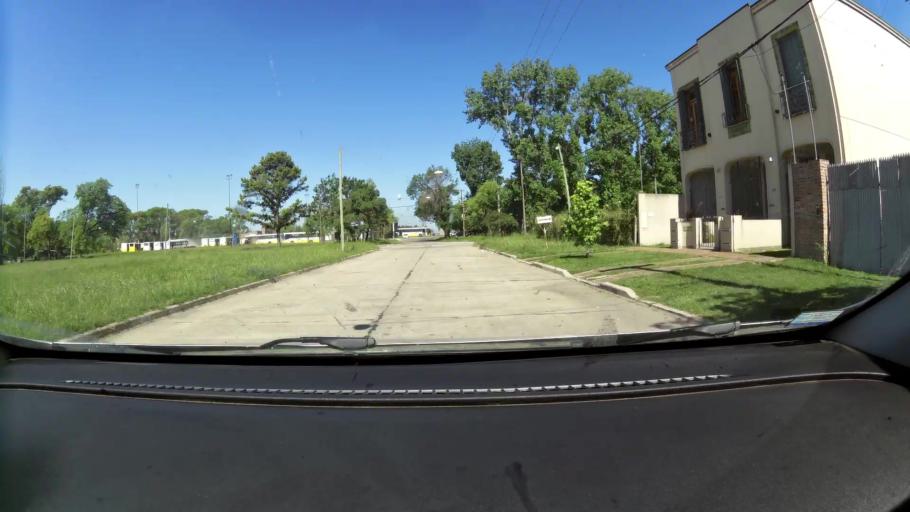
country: AR
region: Santa Fe
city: Santa Fe de la Vera Cruz
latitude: -31.5999
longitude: -60.6673
